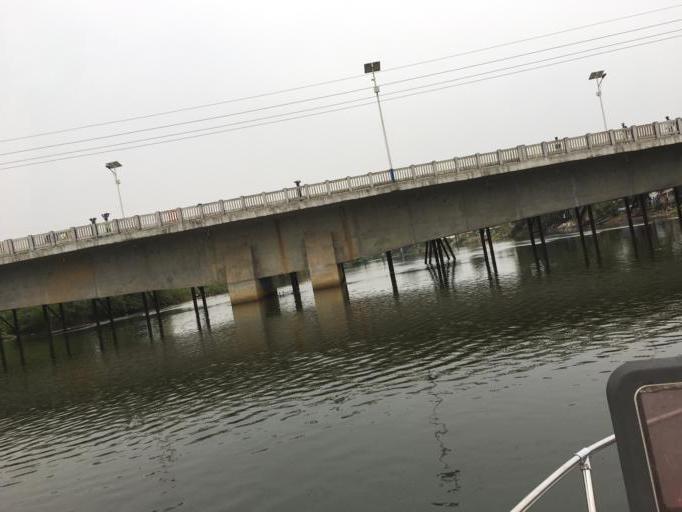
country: LR
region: Montserrado
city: Monrovia
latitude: 6.3733
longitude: -10.7796
